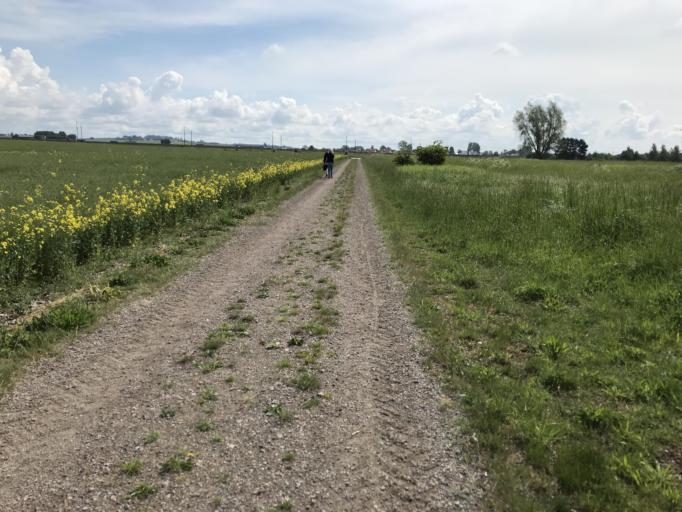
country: SE
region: Skane
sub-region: Landskrona
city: Landskrona
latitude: 55.8991
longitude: 12.8456
